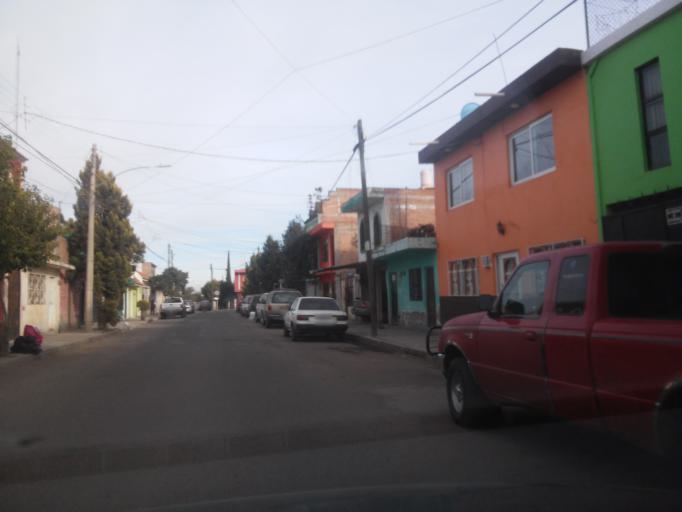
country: MX
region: Durango
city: Victoria de Durango
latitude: 24.0245
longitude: -104.6395
